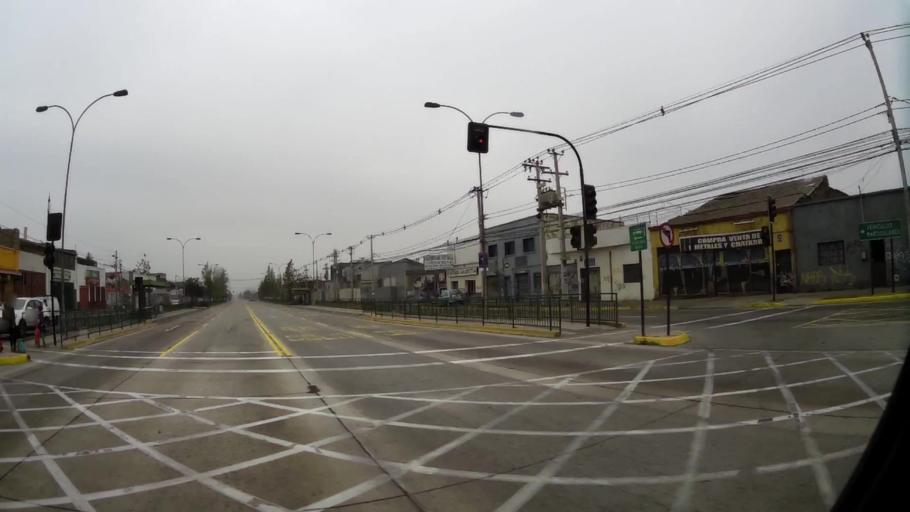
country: CL
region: Santiago Metropolitan
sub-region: Provincia de Santiago
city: Santiago
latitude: -33.4978
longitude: -70.6397
